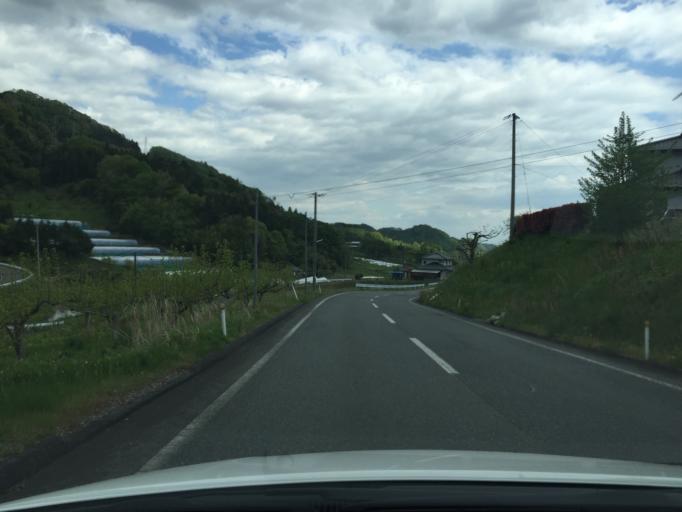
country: JP
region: Fukushima
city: Fukushima-shi
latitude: 37.7245
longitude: 140.5504
